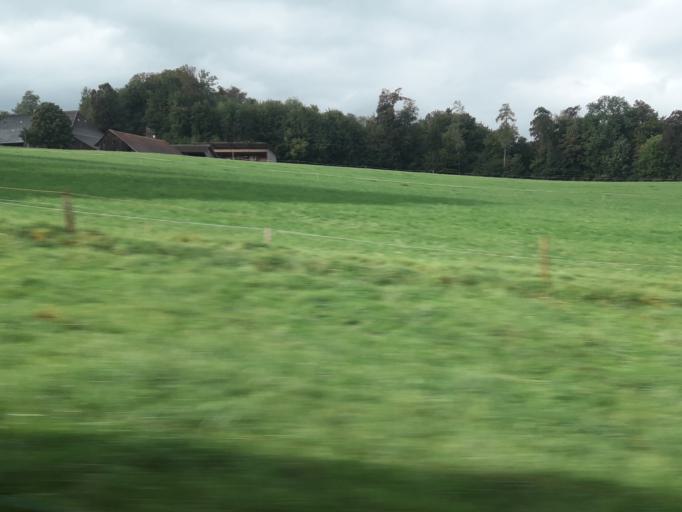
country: CH
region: Bern
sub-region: Thun District
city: Uetendorf
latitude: 46.7828
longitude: 7.5655
